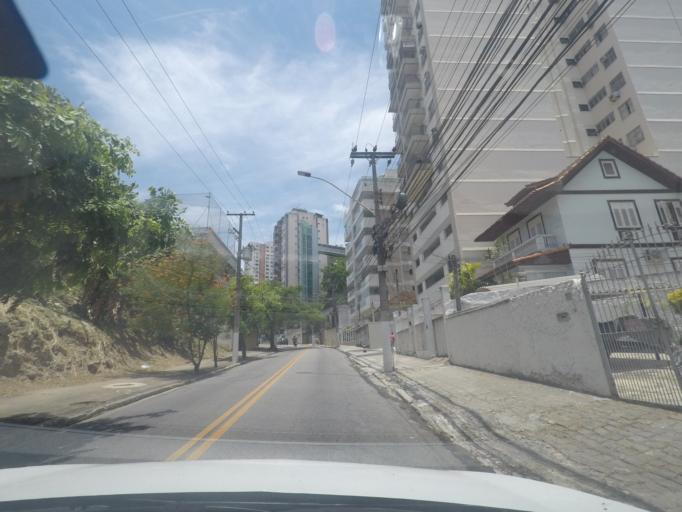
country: BR
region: Rio de Janeiro
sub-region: Niteroi
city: Niteroi
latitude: -22.8997
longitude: -43.1148
